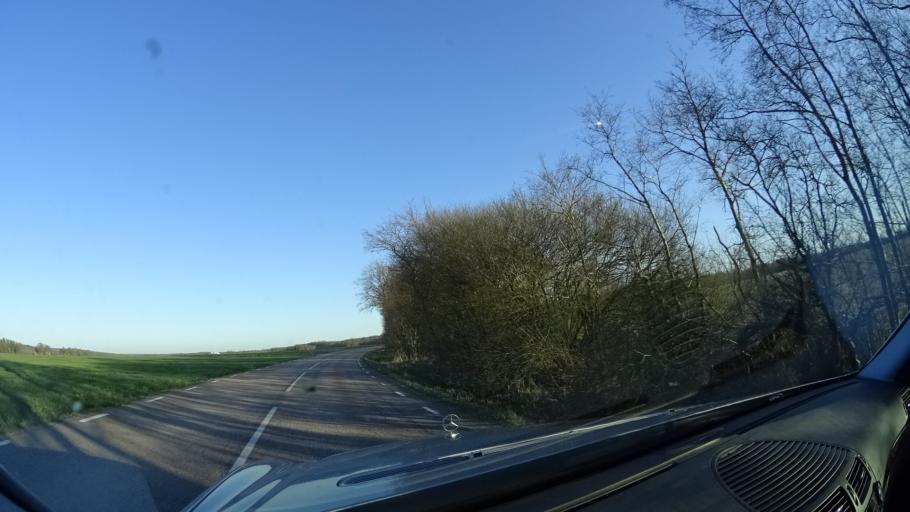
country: SE
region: Skane
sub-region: Bjuvs Kommun
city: Billesholm
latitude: 56.0250
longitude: 13.0456
